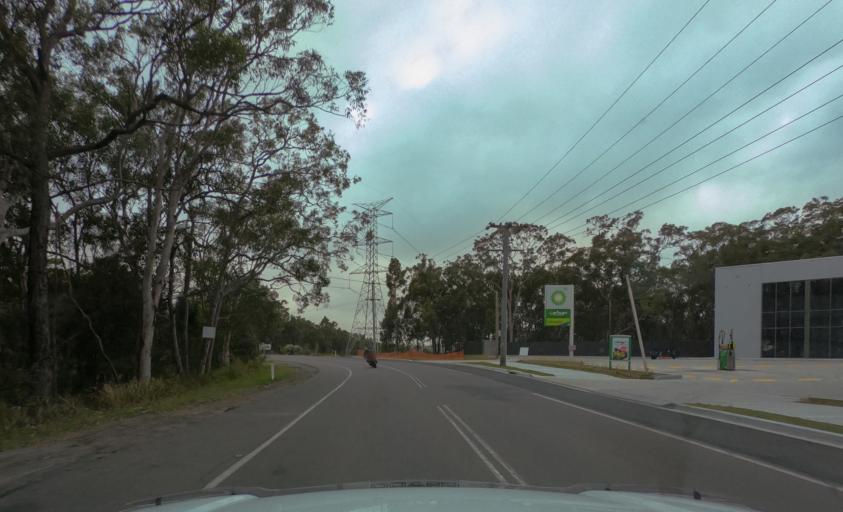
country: AU
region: New South Wales
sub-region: Lake Macquarie Shire
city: Dora Creek
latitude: -33.1077
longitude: 151.4982
